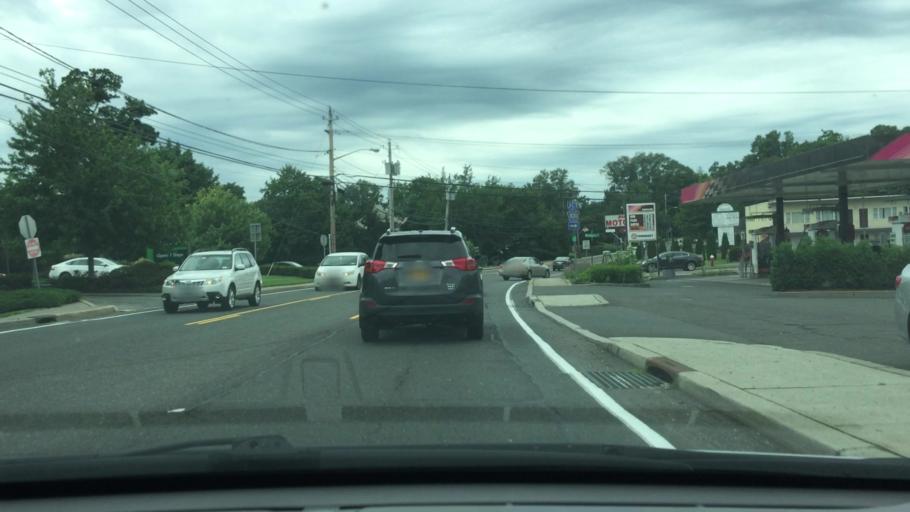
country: US
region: New York
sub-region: Rockland County
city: Stony Point
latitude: 41.2230
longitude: -73.9845
